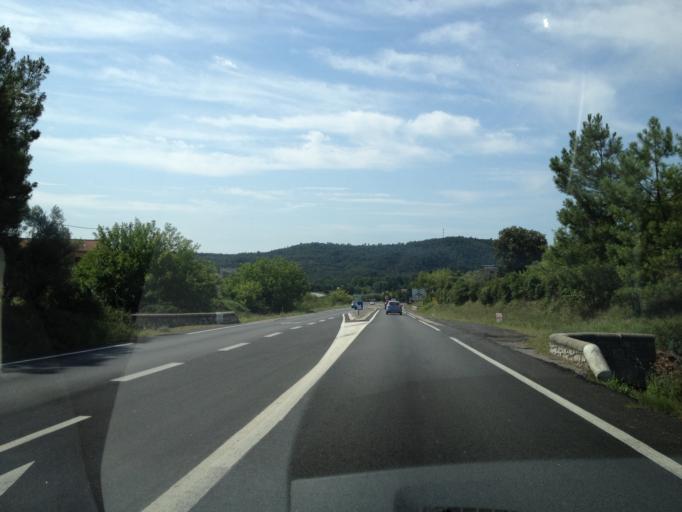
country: FR
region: Languedoc-Roussillon
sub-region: Departement du Gard
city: Les Mages
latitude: 44.2306
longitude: 4.1621
